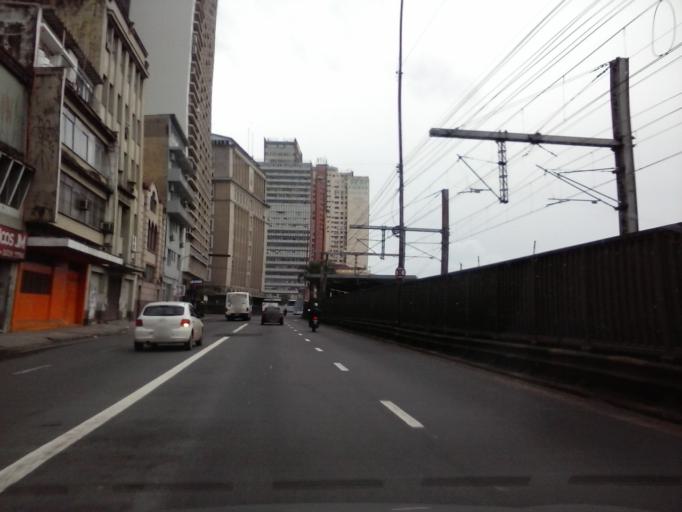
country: BR
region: Rio Grande do Sul
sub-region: Porto Alegre
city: Porto Alegre
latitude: -30.0257
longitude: -51.2261
